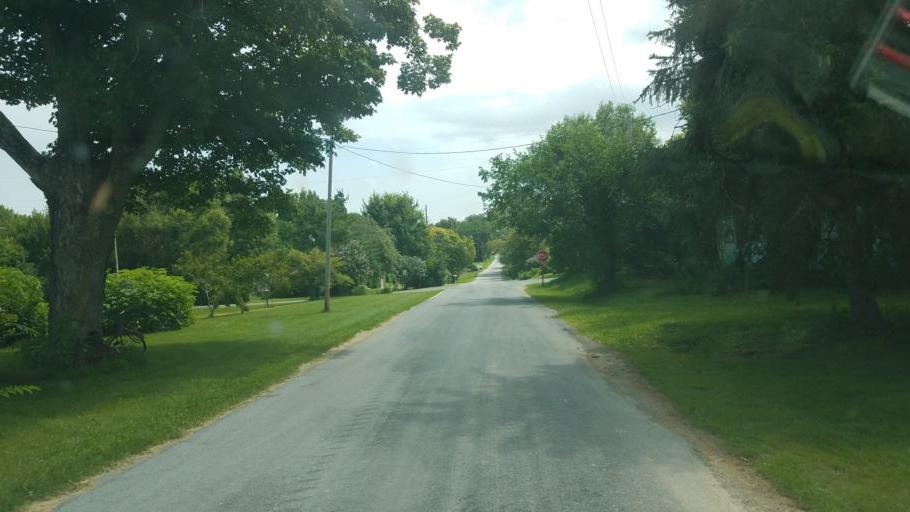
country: US
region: Ohio
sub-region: Wyandot County
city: Upper Sandusky
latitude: 40.8770
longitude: -83.1516
